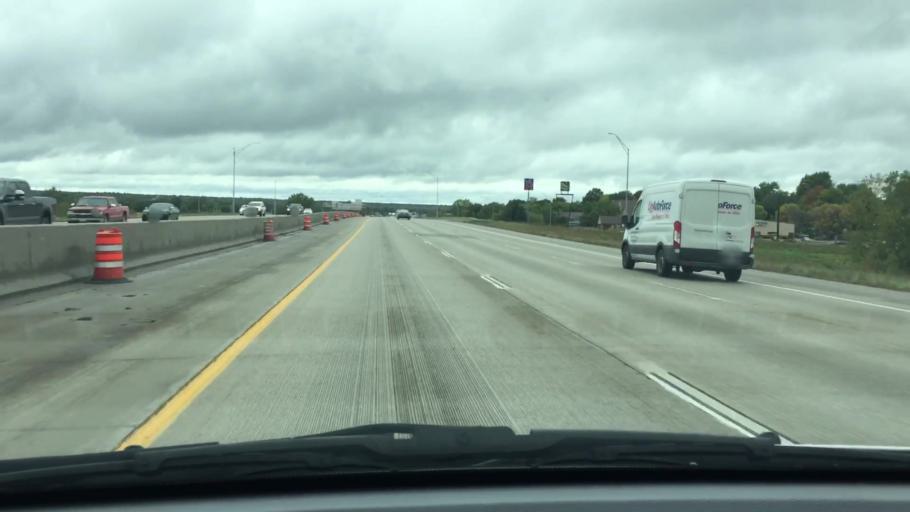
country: US
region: Iowa
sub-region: Polk County
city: Saylorville
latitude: 41.6502
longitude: -93.5975
